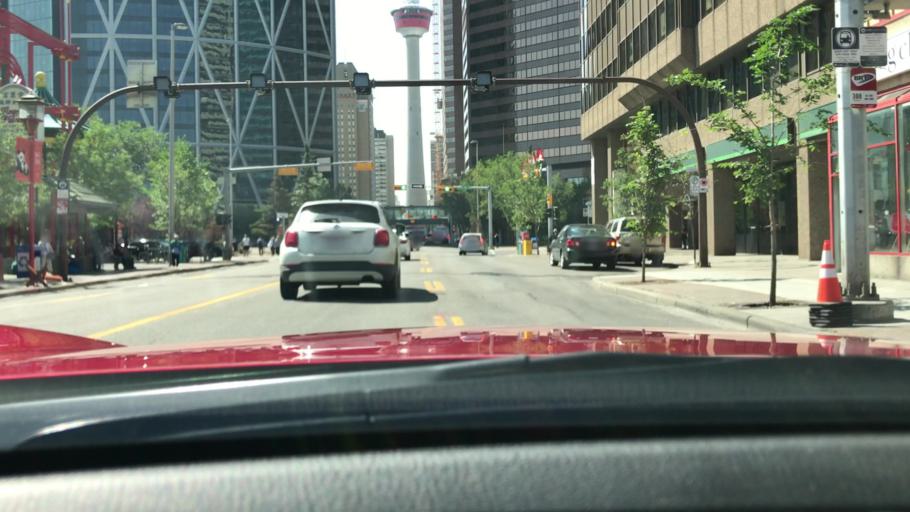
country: CA
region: Alberta
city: Calgary
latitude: 51.0500
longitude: -114.0628
